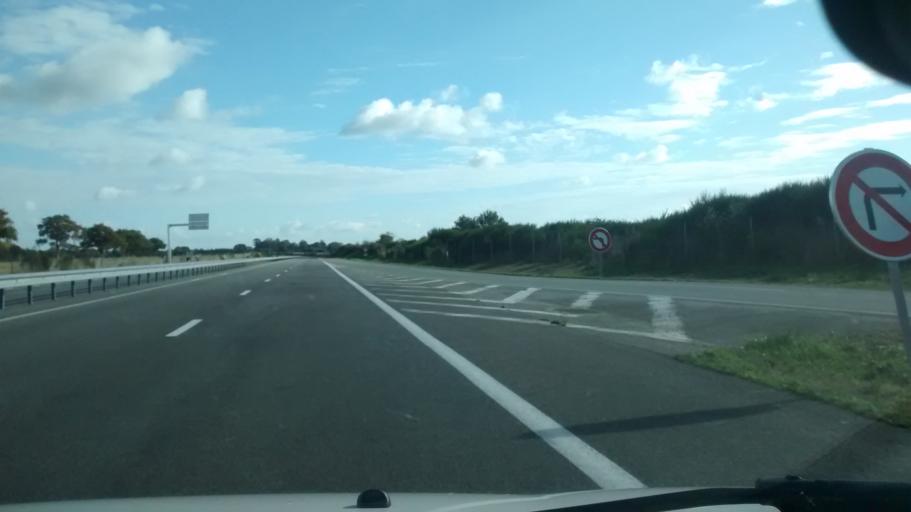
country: FR
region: Pays de la Loire
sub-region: Departement de Maine-et-Loire
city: Pouance
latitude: 47.7295
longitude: -1.1058
